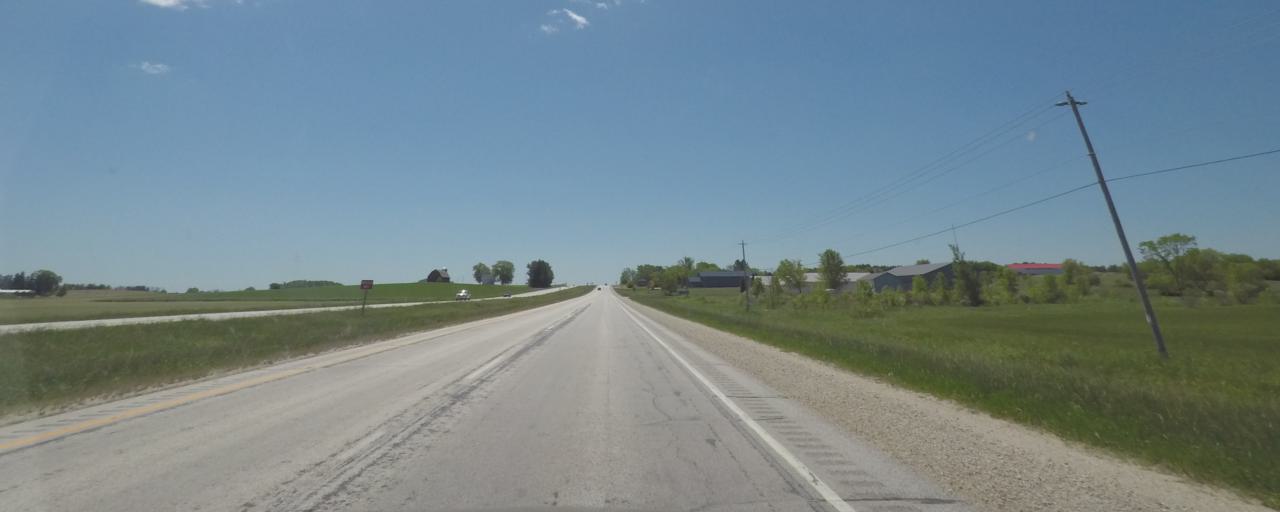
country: US
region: Wisconsin
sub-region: Sheboygan County
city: Plymouth
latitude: 43.6949
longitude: -87.9409
